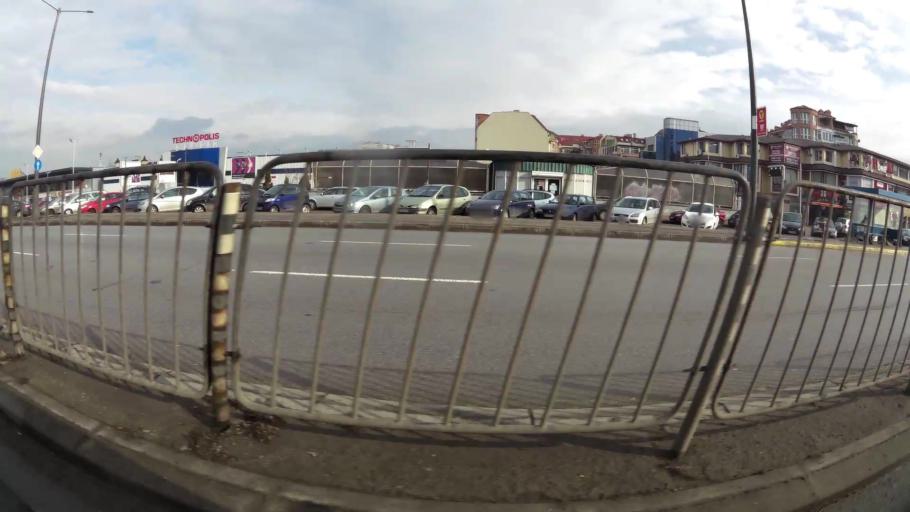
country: BG
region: Sofiya
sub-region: Obshtina Bozhurishte
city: Bozhurishte
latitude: 42.7185
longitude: 23.2572
